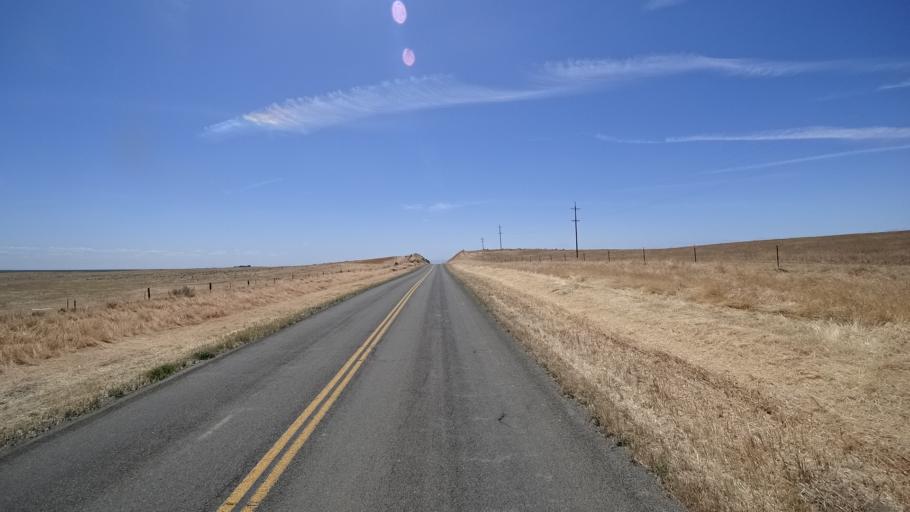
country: US
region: California
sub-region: Kings County
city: Kettleman City
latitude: 35.8926
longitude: -119.9151
